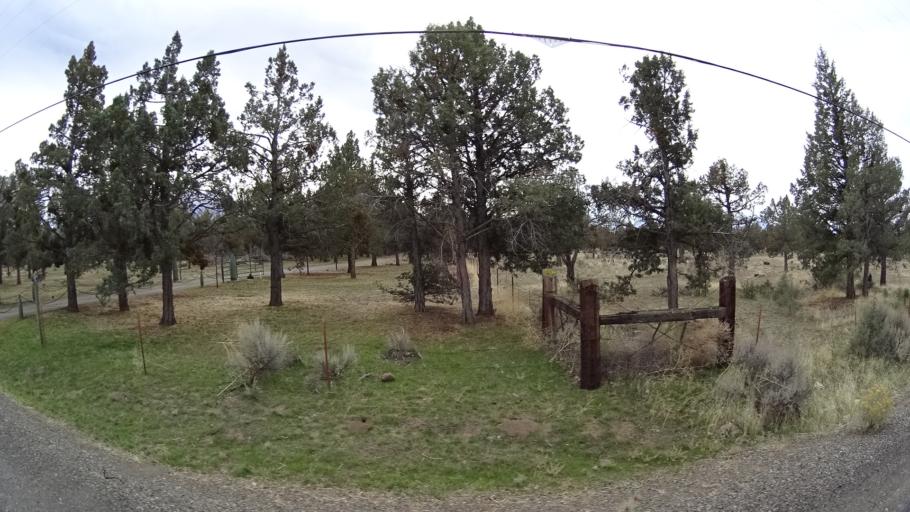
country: US
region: California
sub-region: Siskiyou County
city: Weed
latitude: 41.5936
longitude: -122.3162
